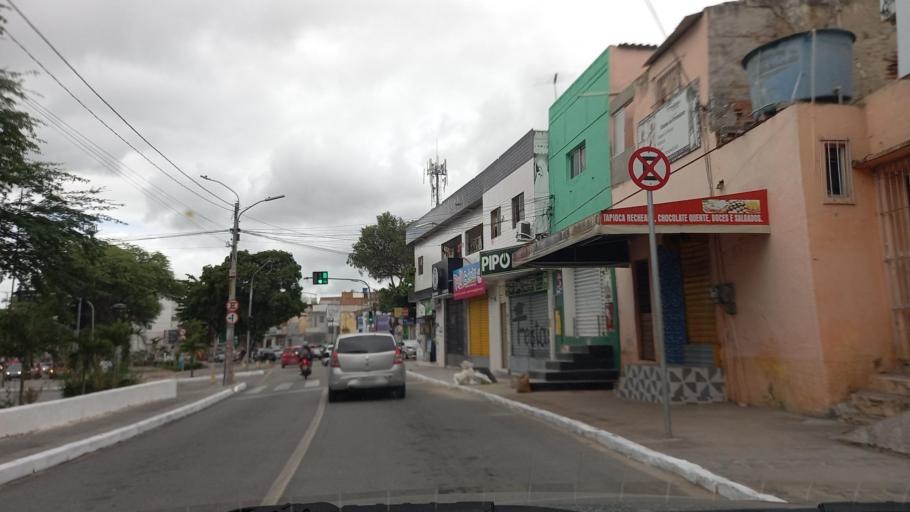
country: BR
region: Pernambuco
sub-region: Caruaru
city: Caruaru
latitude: -8.2818
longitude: -35.9735
